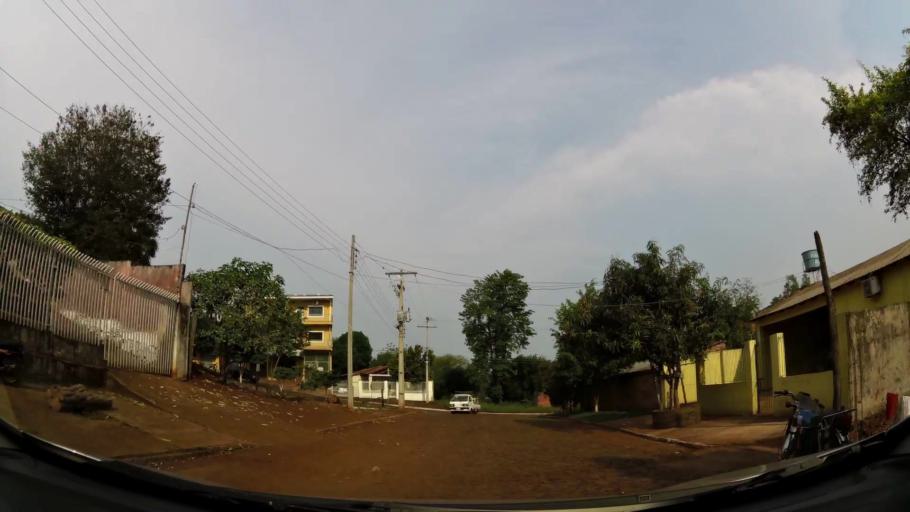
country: PY
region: Alto Parana
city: Ciudad del Este
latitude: -25.4936
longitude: -54.6544
